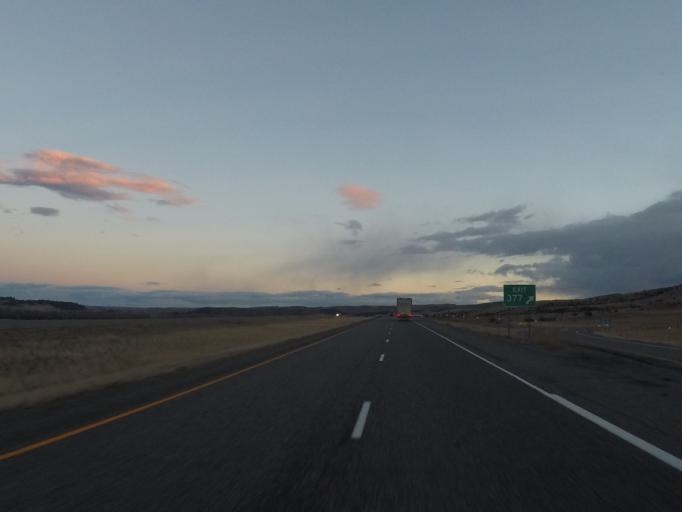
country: US
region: Montana
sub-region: Sweet Grass County
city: Big Timber
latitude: 45.7714
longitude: -109.7958
